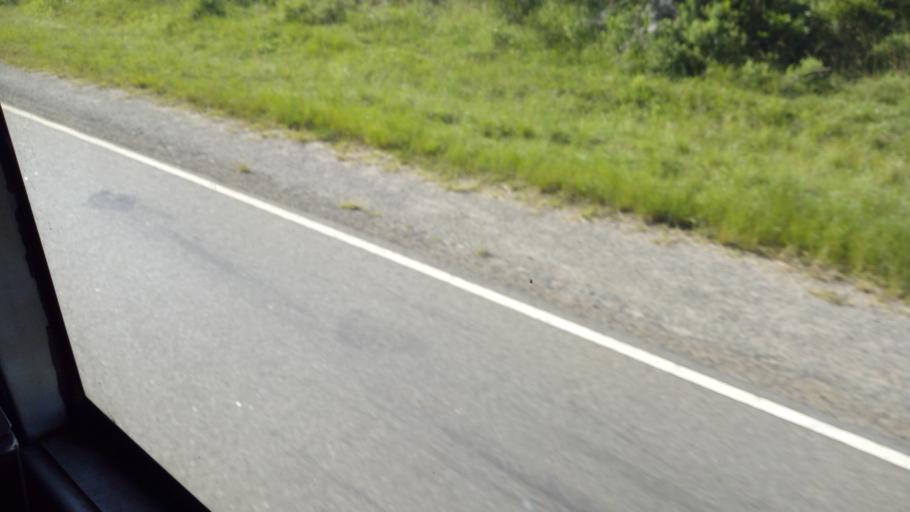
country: UG
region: Central Region
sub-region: Lyantonde District
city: Lyantonde
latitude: -0.4561
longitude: 31.0498
